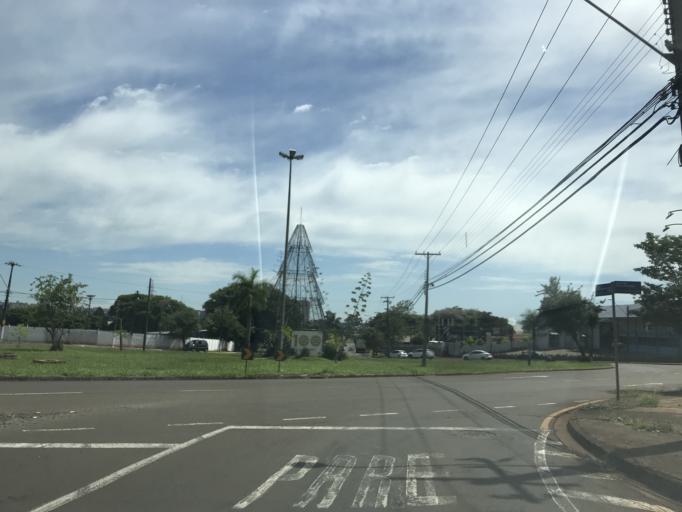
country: BR
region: Parana
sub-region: Londrina
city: Londrina
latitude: -23.3459
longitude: -51.1633
